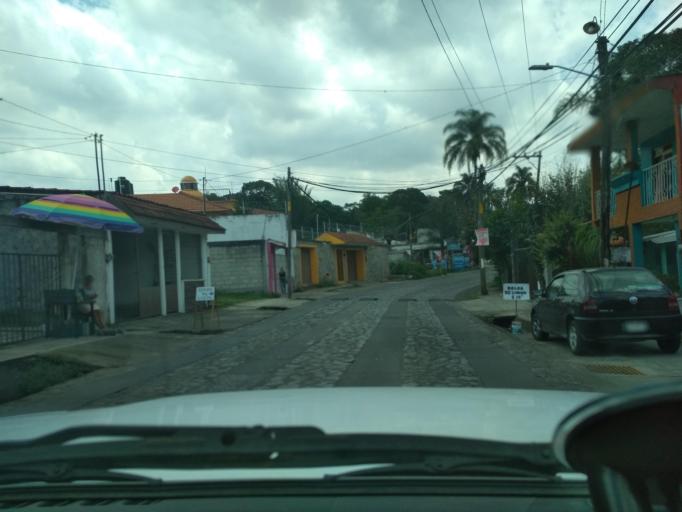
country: MX
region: Veracruz
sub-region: Cordoba
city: San Jose de Abajo [Unidad Habitacional]
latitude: 18.9096
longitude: -96.9600
